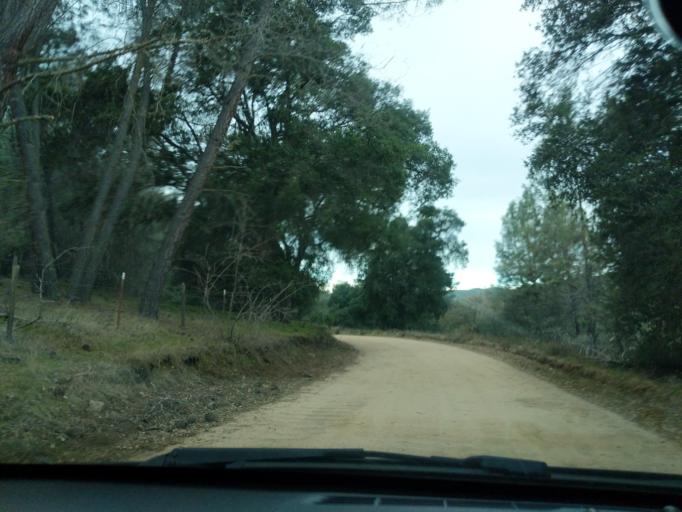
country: US
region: California
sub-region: Monterey County
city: Soledad
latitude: 36.5652
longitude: -121.2177
